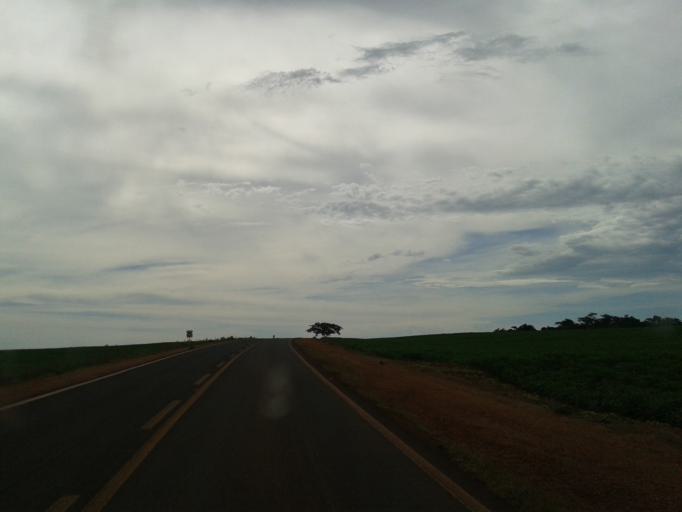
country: BR
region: Minas Gerais
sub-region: Capinopolis
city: Capinopolis
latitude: -18.6927
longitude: -49.4753
